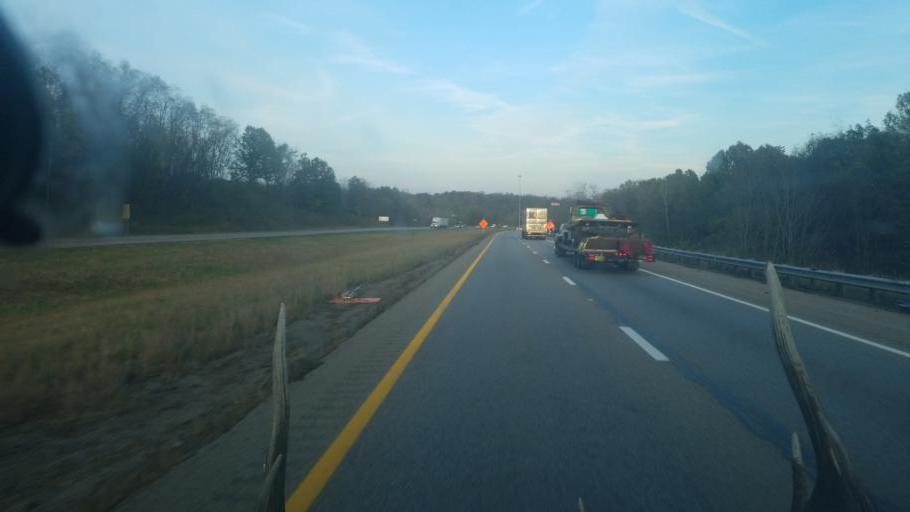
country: US
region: Ohio
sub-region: Muskingum County
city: Zanesville
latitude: 39.9484
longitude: -82.0631
